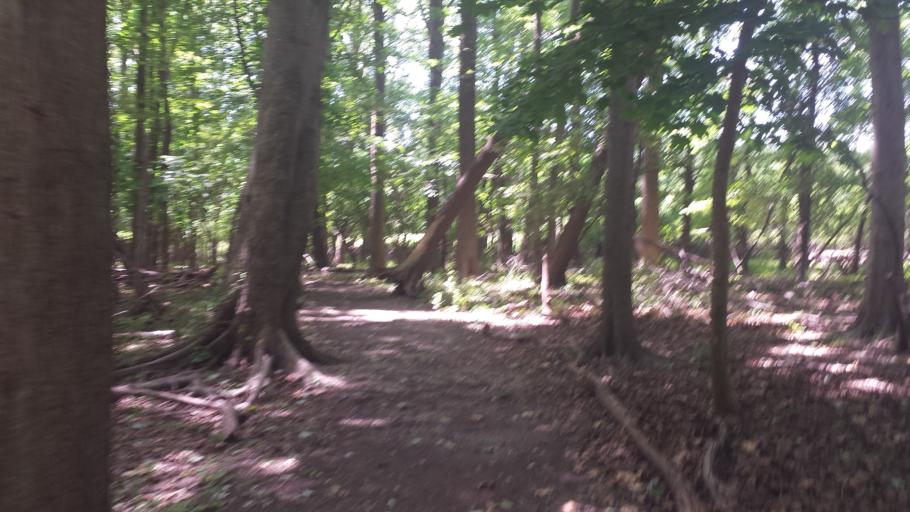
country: US
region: New York
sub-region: Westchester County
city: Harrison
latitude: 40.9551
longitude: -73.7036
